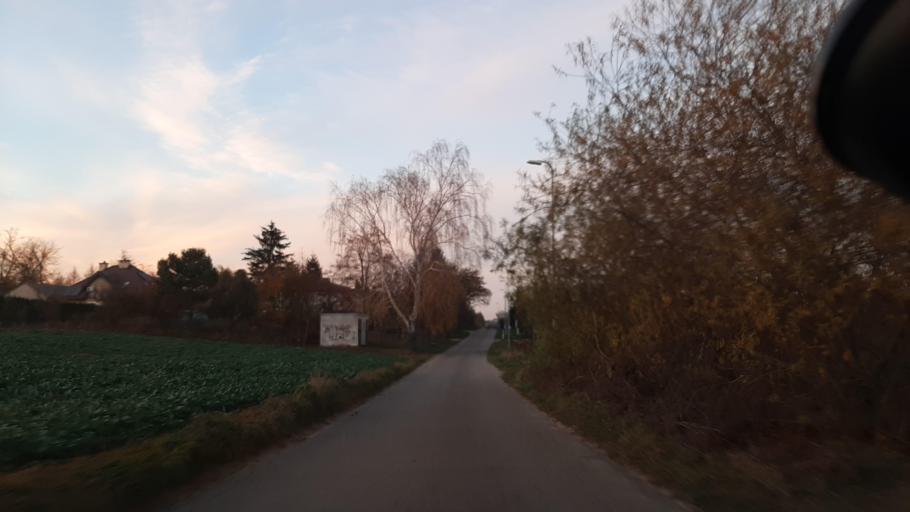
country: PL
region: Lublin Voivodeship
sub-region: Powiat lubelski
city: Jastkow
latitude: 51.2970
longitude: 22.5043
